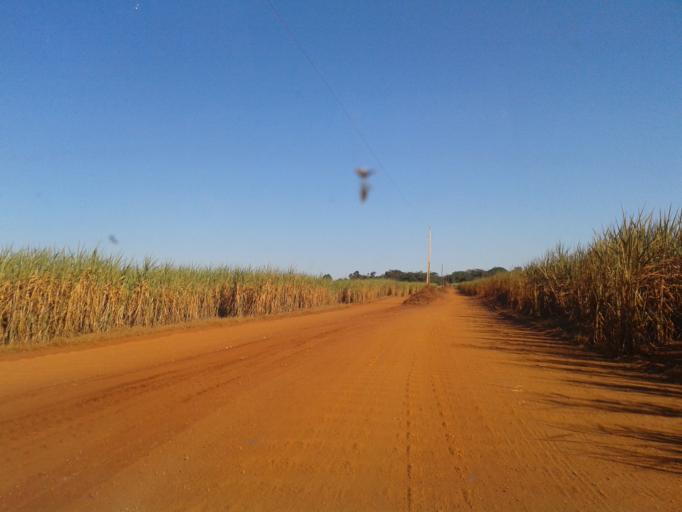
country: BR
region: Minas Gerais
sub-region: Santa Vitoria
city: Santa Vitoria
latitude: -18.8673
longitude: -50.0494
